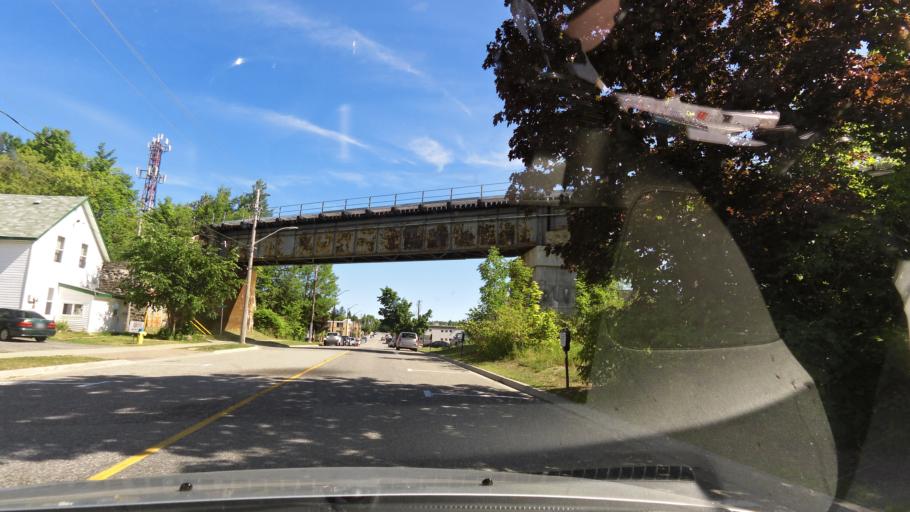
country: CA
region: Ontario
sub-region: Parry Sound District
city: Parry Sound
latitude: 45.3417
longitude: -80.0352
